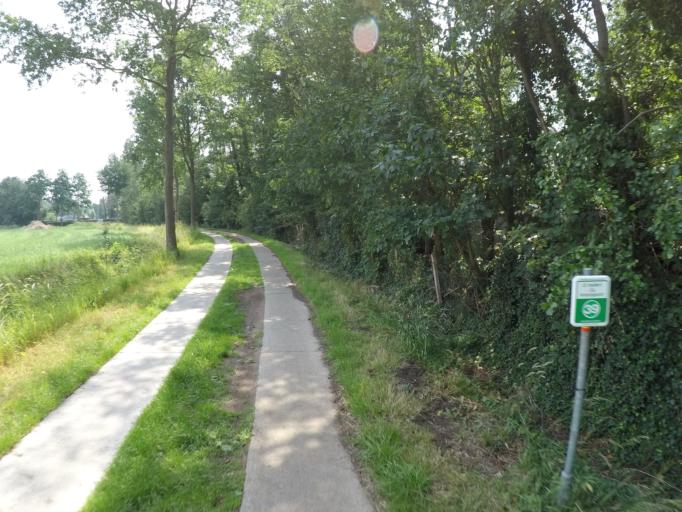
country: BE
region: Flanders
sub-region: Provincie Antwerpen
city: Rijkevorsel
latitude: 51.3547
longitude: 4.7385
